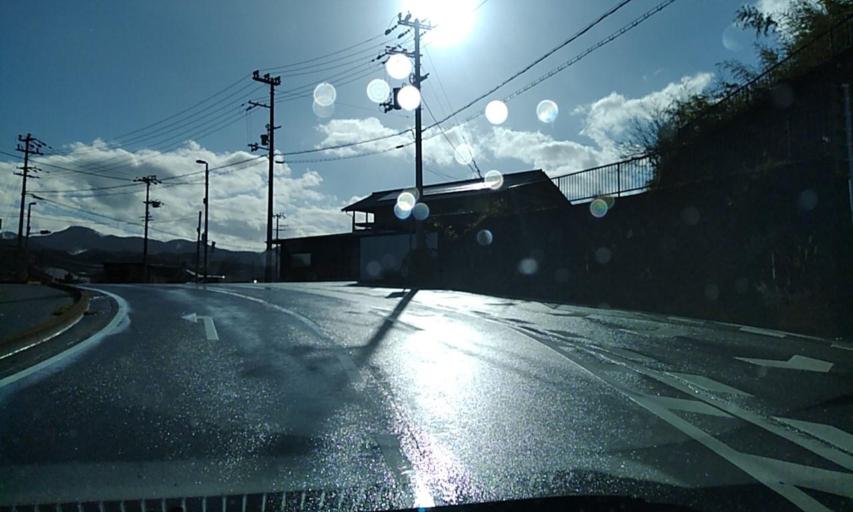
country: JP
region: Kyoto
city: Fukuchiyama
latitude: 35.3946
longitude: 135.1504
